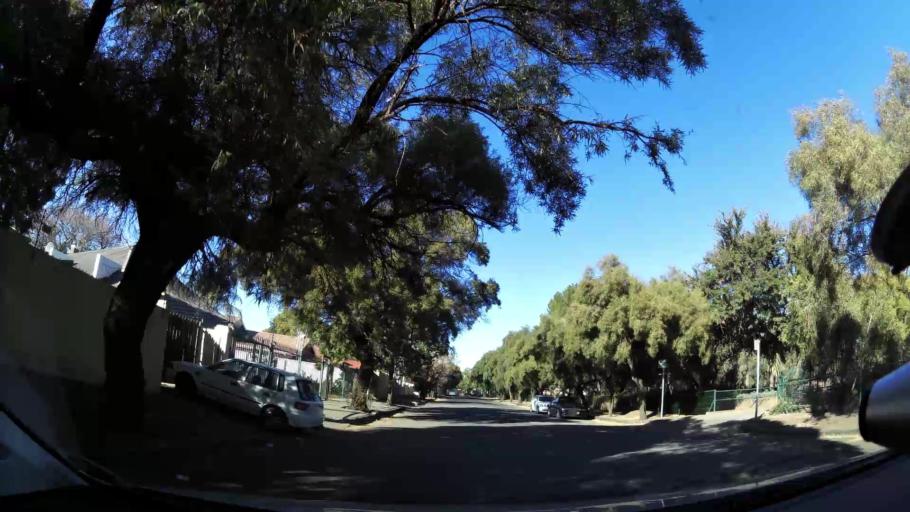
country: ZA
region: Northern Cape
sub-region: Frances Baard District Municipality
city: Kimberley
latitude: -28.7424
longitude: 24.7764
